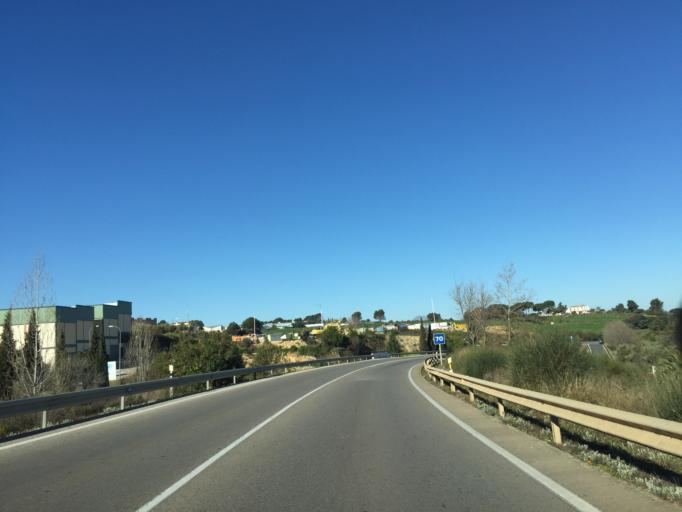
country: ES
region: Andalusia
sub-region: Provincia de Malaga
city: Ronda
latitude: 36.7551
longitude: -5.1521
